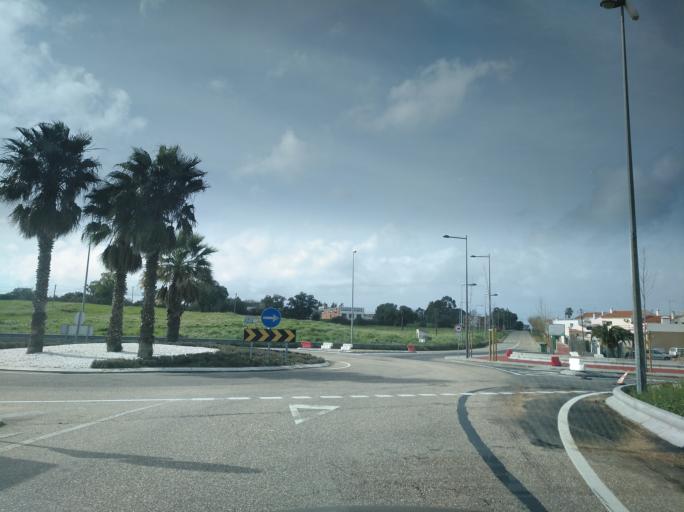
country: PT
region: Setubal
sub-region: Grandola
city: Grandola
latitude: 38.1694
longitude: -8.5545
